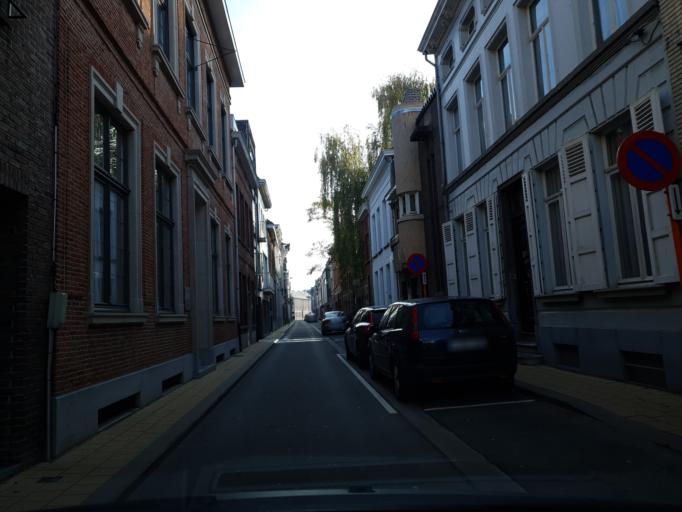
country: BE
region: Flanders
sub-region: Provincie Oost-Vlaanderen
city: Sint-Niklaas
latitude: 51.1635
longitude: 4.1457
